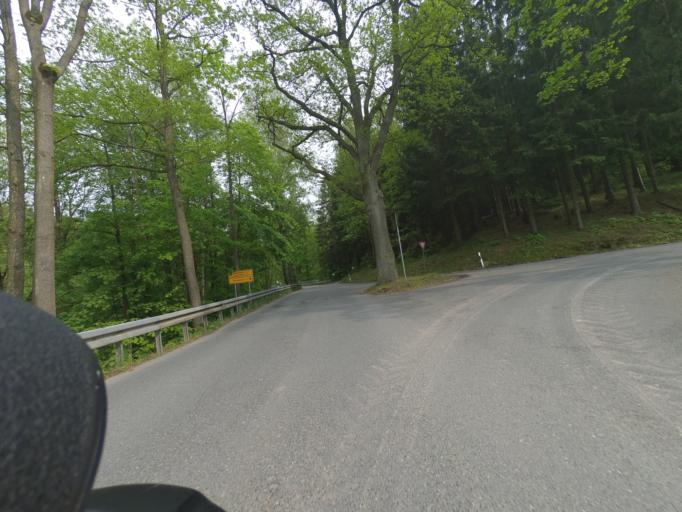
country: DE
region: Saxony
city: Obercunnersdorf
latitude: 50.8786
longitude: 13.5672
